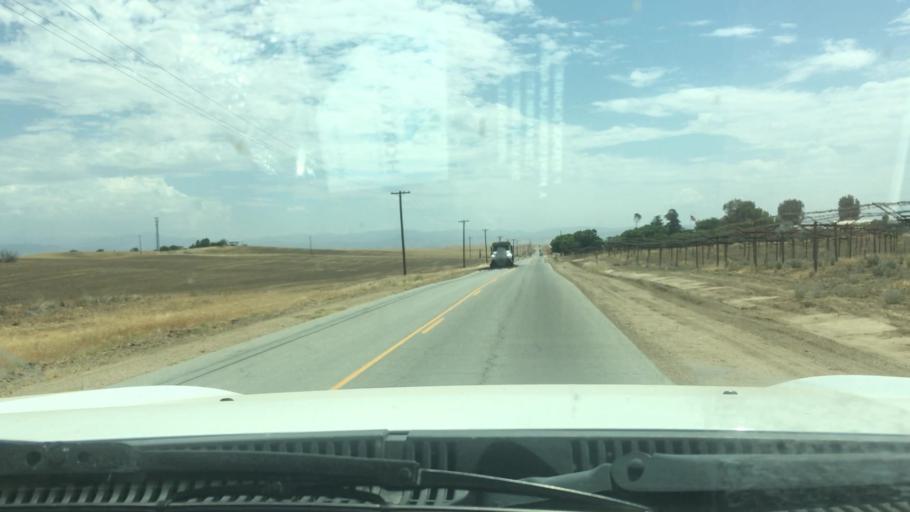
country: US
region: California
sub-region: Kern County
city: McFarland
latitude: 35.6025
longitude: -119.0952
